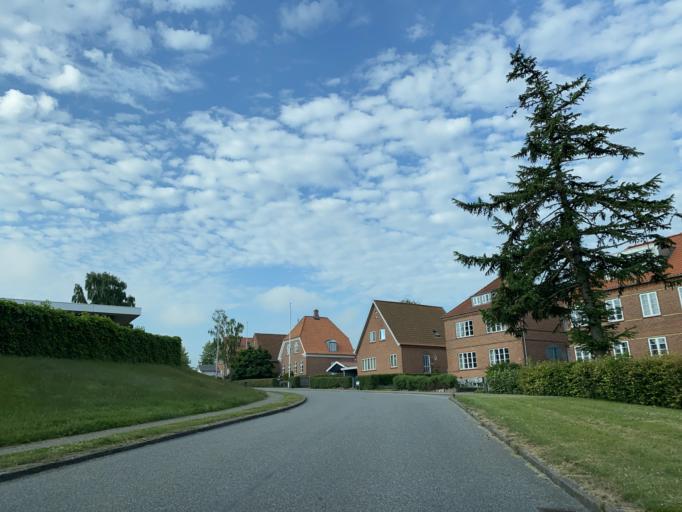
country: DK
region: South Denmark
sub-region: Haderslev Kommune
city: Haderslev
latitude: 55.2450
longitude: 9.4921
